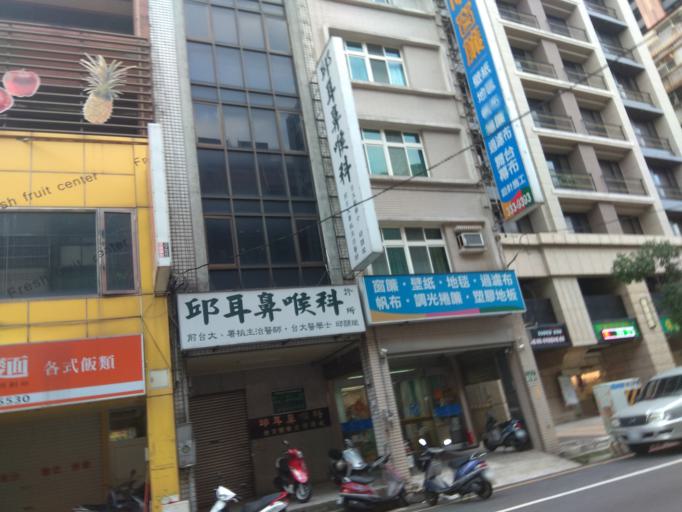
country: TW
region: Taiwan
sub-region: Taoyuan
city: Taoyuan
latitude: 24.9936
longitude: 121.3084
